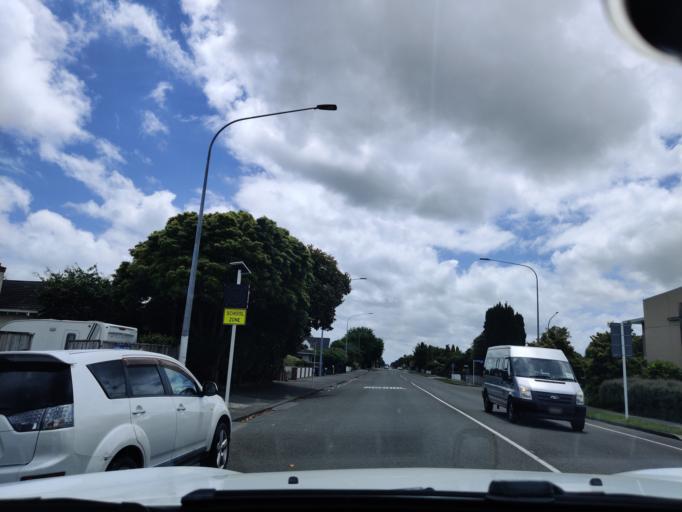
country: NZ
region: Manawatu-Wanganui
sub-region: Palmerston North City
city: Palmerston North
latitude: -40.3622
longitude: 175.6333
